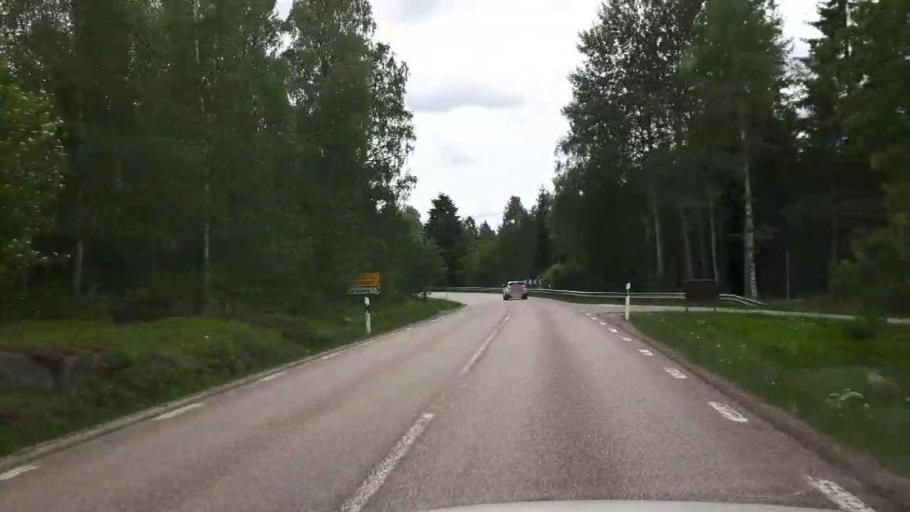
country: SE
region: Vaestmanland
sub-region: Norbergs Kommun
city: Norberg
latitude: 60.1135
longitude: 15.9189
